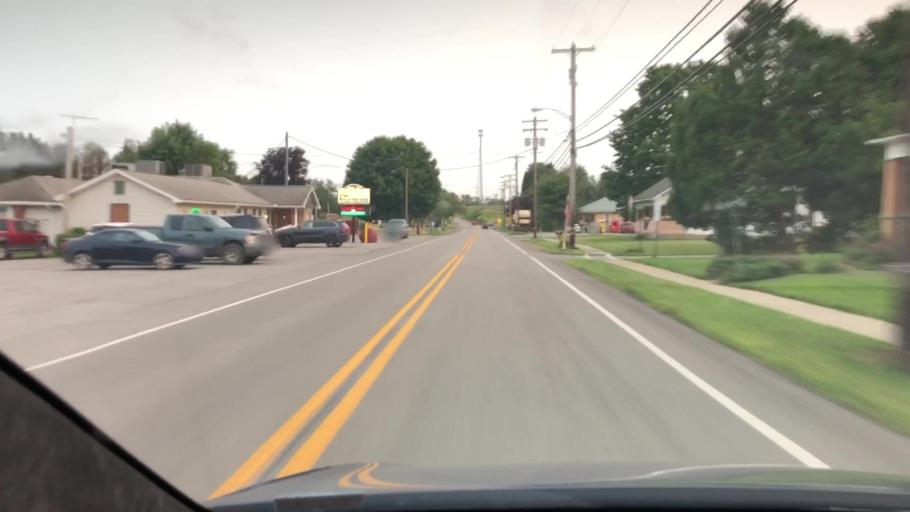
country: US
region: Pennsylvania
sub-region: Butler County
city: Slippery Rock
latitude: 41.1310
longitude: -80.0089
